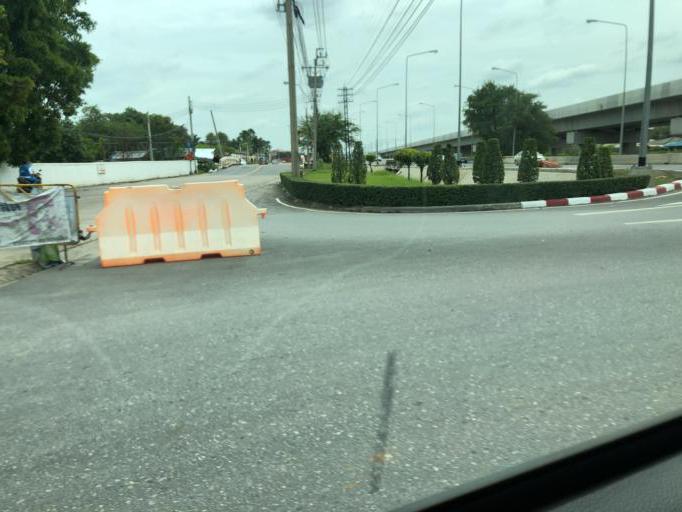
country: TH
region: Bangkok
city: Don Mueang
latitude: 13.9386
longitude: 100.6082
